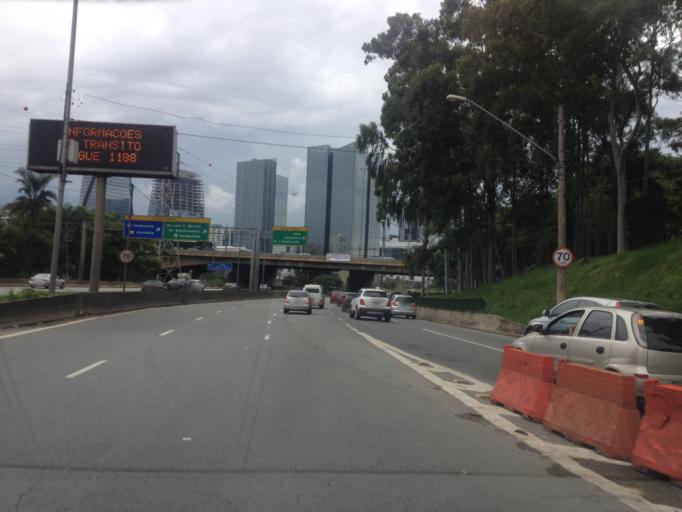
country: BR
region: Sao Paulo
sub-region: Sao Paulo
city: Sao Paulo
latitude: -23.5854
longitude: -46.6926
